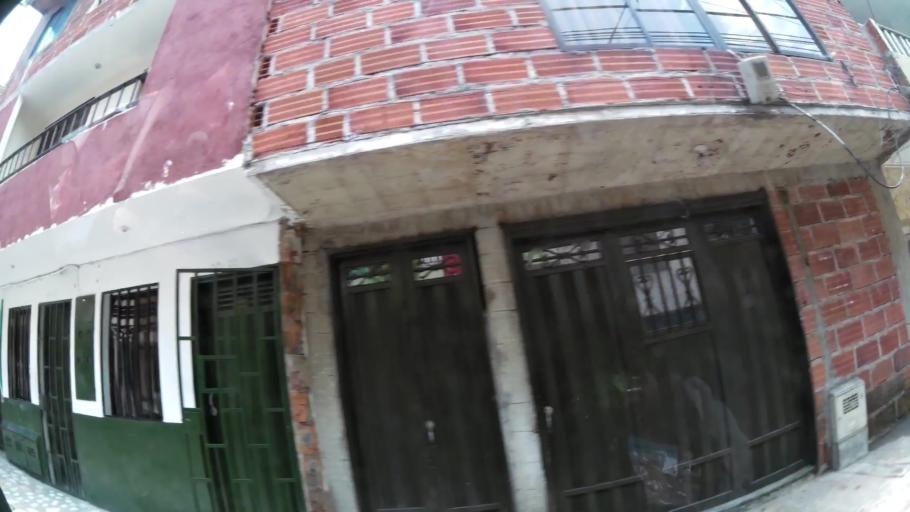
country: CO
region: Antioquia
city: Sabaneta
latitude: 6.1647
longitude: -75.6140
